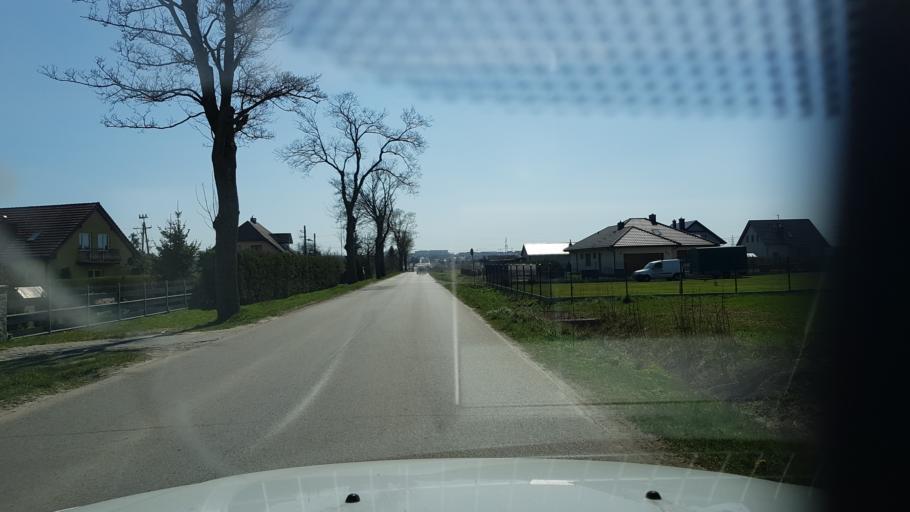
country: PL
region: West Pomeranian Voivodeship
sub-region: Koszalin
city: Koszalin
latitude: 54.2389
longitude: 16.1770
